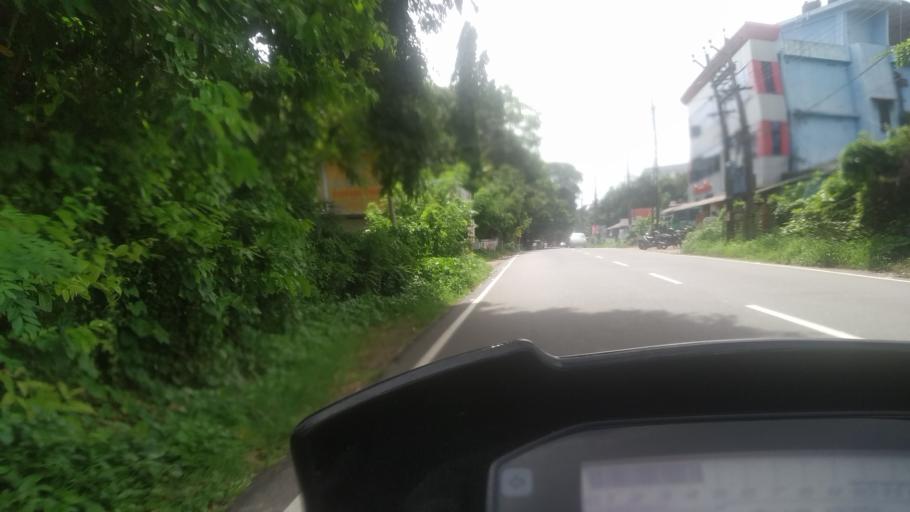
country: IN
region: Kerala
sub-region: Ernakulam
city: Elur
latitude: 10.1403
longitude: 76.2645
